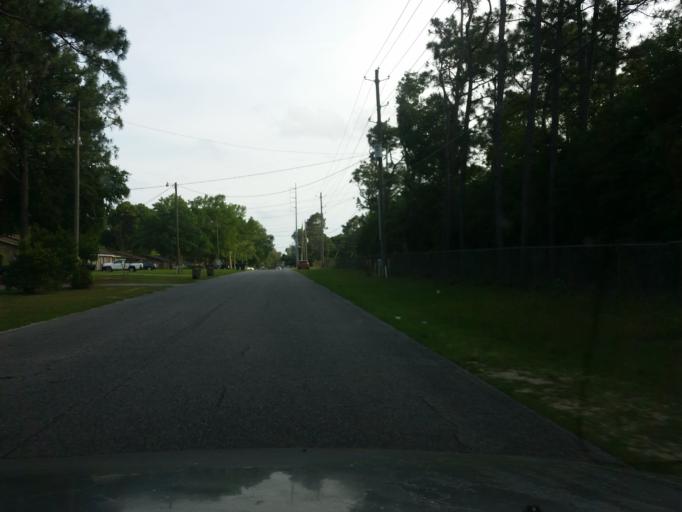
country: US
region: Florida
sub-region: Escambia County
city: Ferry Pass
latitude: 30.4996
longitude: -87.2049
